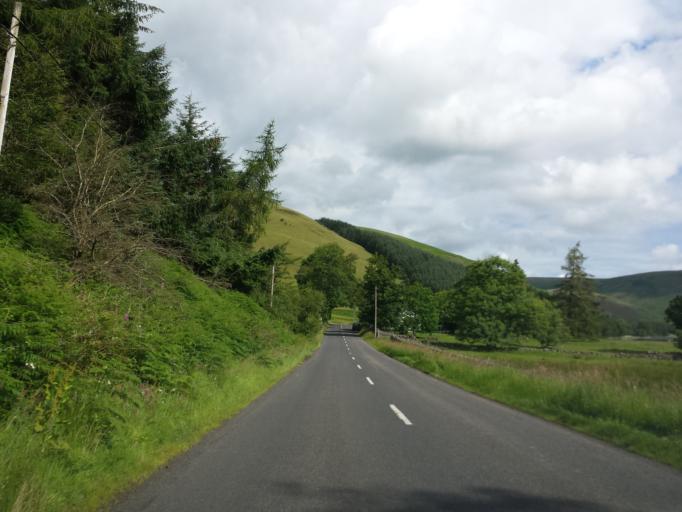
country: GB
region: Scotland
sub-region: The Scottish Borders
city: Peebles
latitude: 55.4761
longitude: -3.2079
